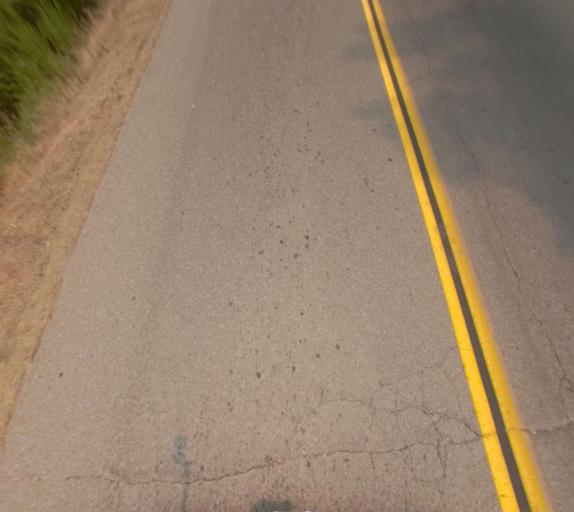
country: US
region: California
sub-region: Madera County
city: Oakhurst
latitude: 37.3279
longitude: -119.6604
